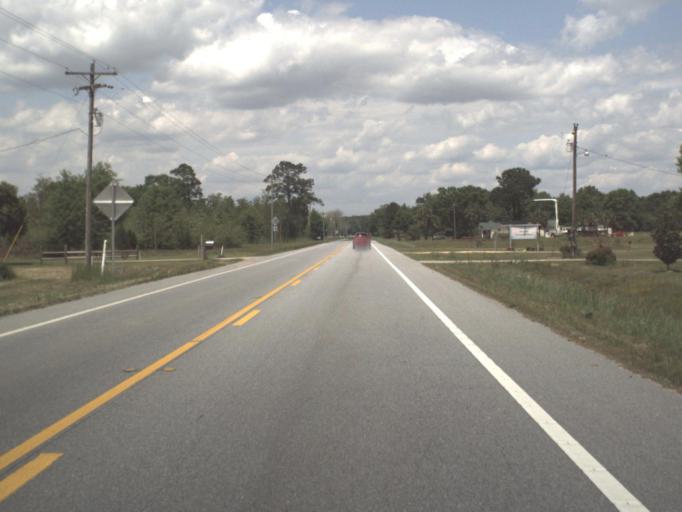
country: US
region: Alabama
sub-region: Escambia County
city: Atmore
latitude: 30.9540
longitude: -87.4865
